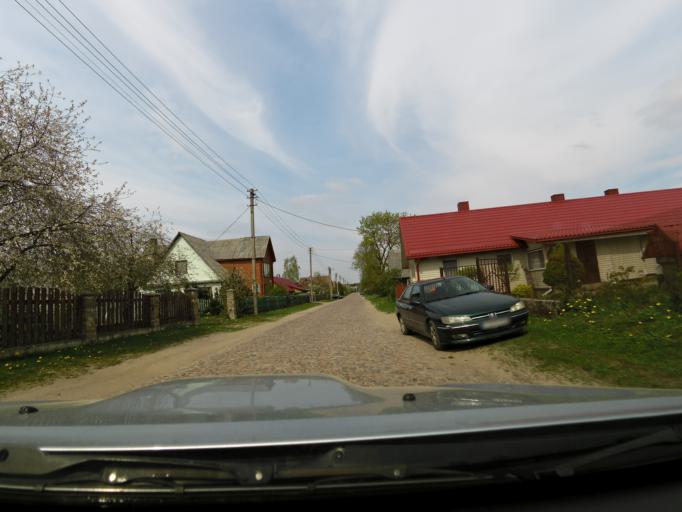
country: LT
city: Baltoji Voke
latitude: 54.4333
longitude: 25.1500
